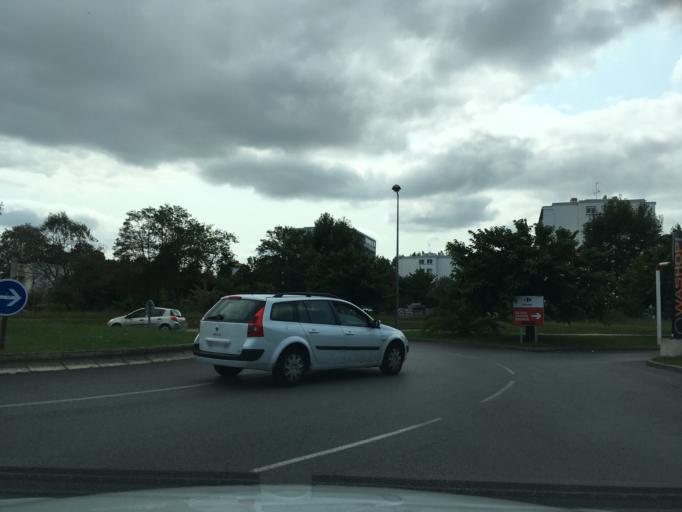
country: FR
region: Aquitaine
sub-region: Departement des Pyrenees-Atlantiques
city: Anglet
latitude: 43.4862
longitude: -1.5005
